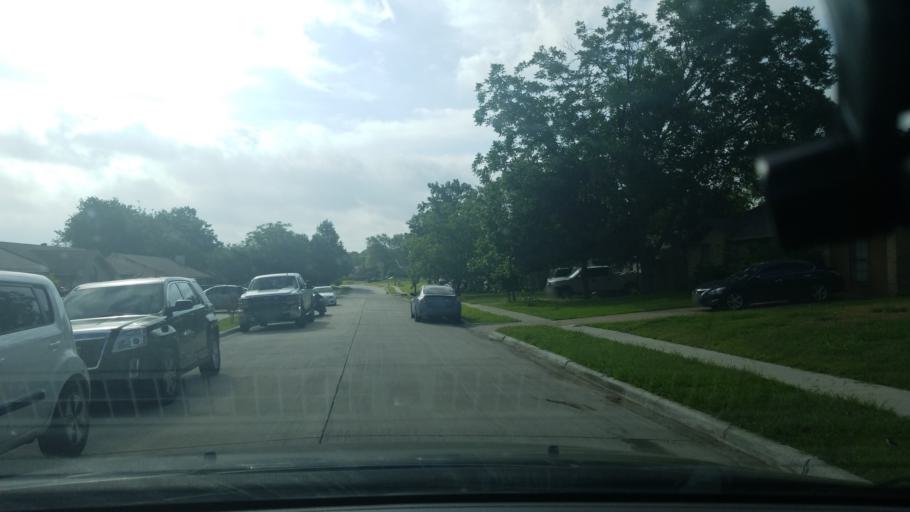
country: US
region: Texas
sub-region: Dallas County
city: Mesquite
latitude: 32.7743
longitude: -96.6413
